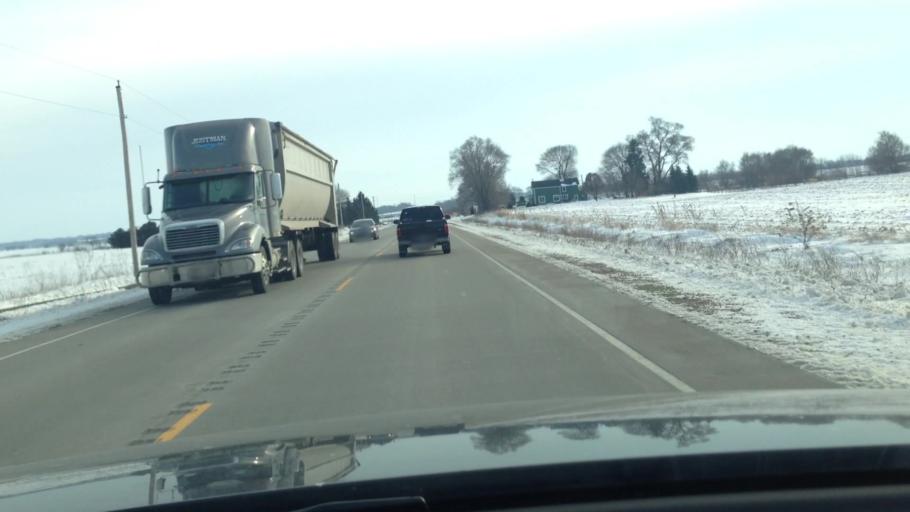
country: US
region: Illinois
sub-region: McHenry County
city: Hebron
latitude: 42.5113
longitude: -88.4427
